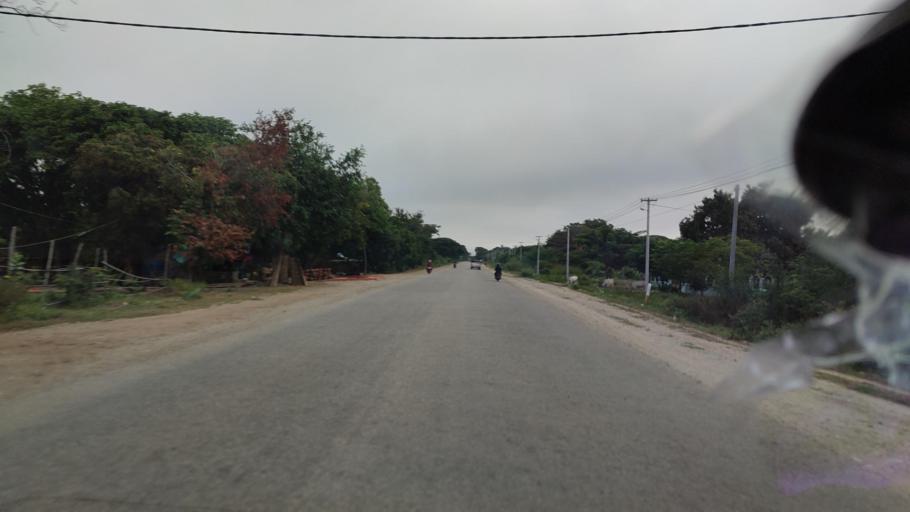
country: MM
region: Mandalay
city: Yamethin
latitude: 20.7243
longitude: 96.1961
